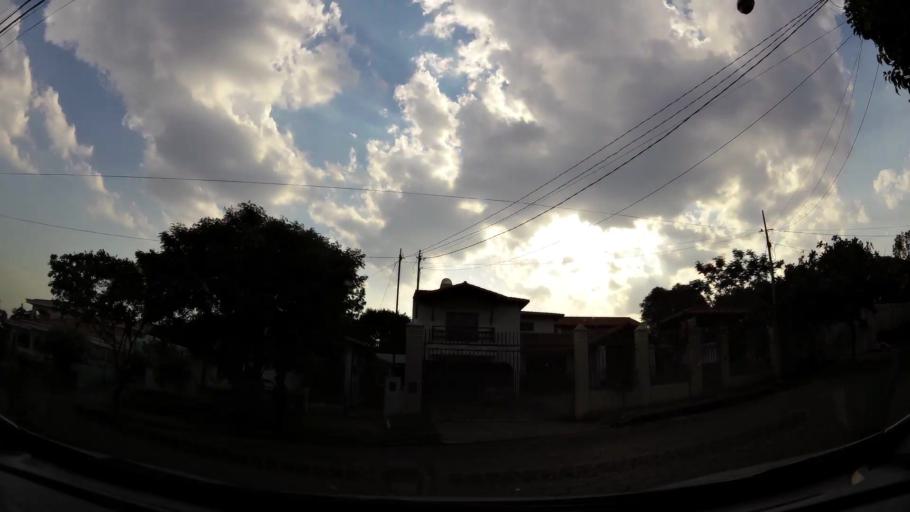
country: PY
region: Alto Parana
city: Presidente Franco
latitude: -25.5227
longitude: -54.6377
